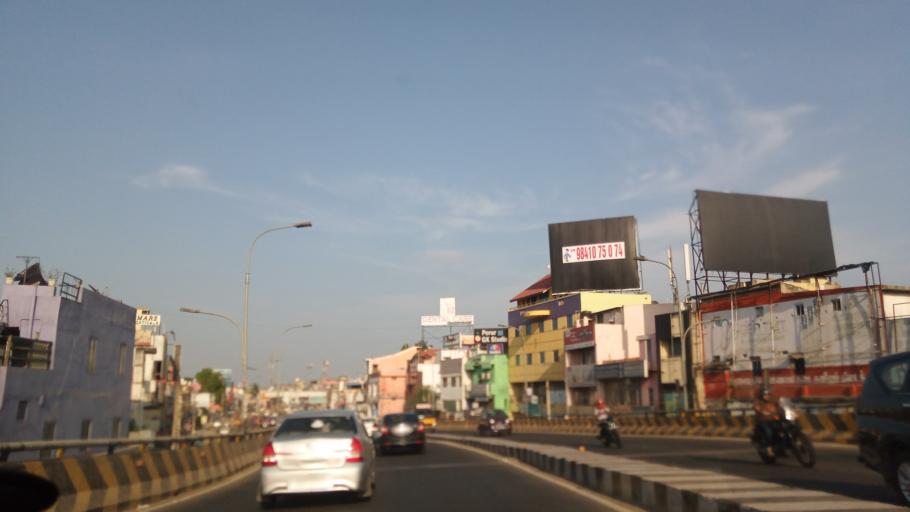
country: IN
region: Tamil Nadu
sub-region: Thiruvallur
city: Porur
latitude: 13.0344
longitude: 80.1568
